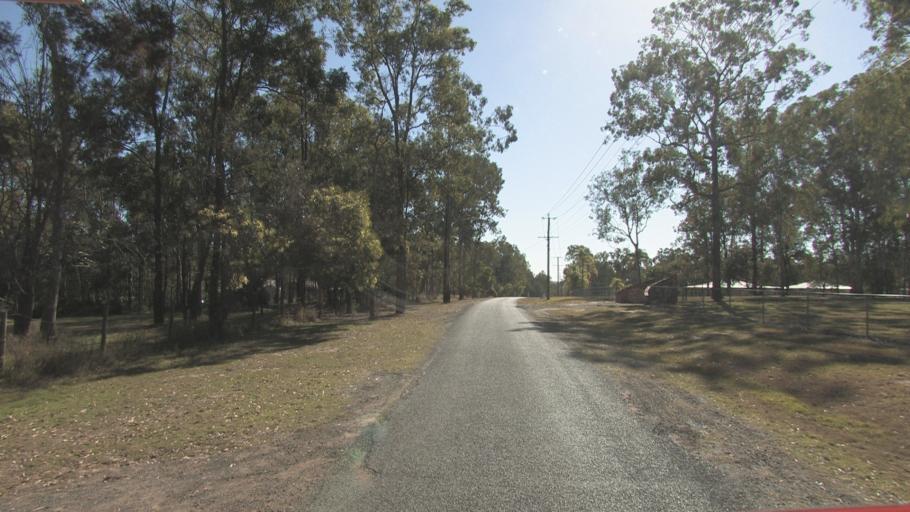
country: AU
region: Queensland
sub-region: Logan
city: Park Ridge South
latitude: -27.7519
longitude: 153.0473
